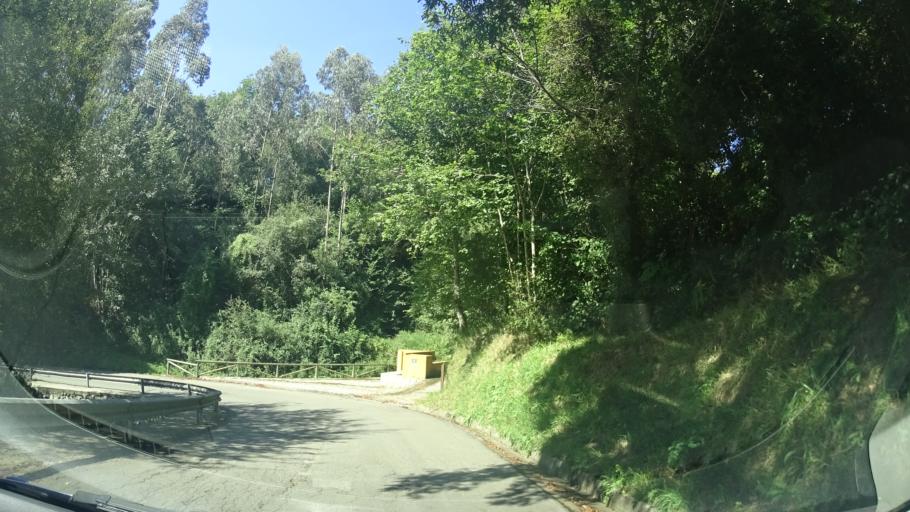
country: ES
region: Asturias
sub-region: Province of Asturias
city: Ribadesella
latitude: 43.4432
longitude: -5.0902
